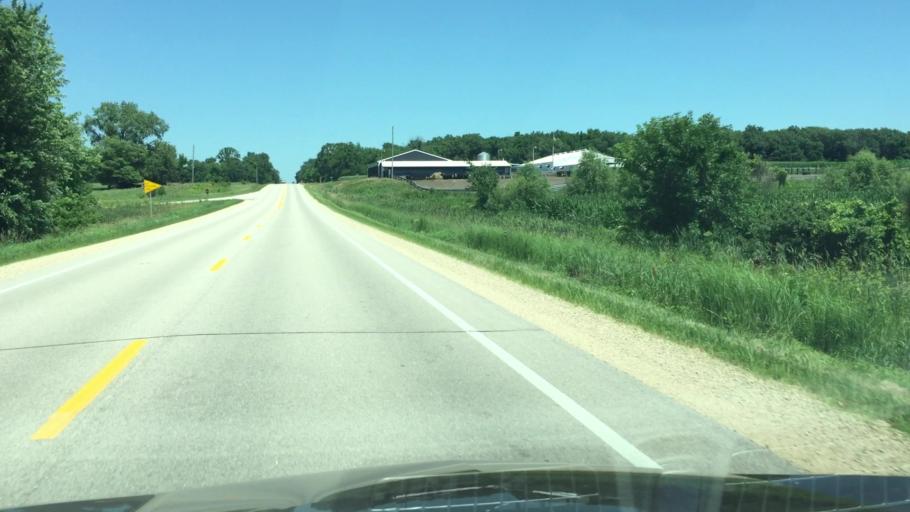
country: US
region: Iowa
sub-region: Cedar County
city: Mechanicsville
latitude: 42.0218
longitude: -91.1367
